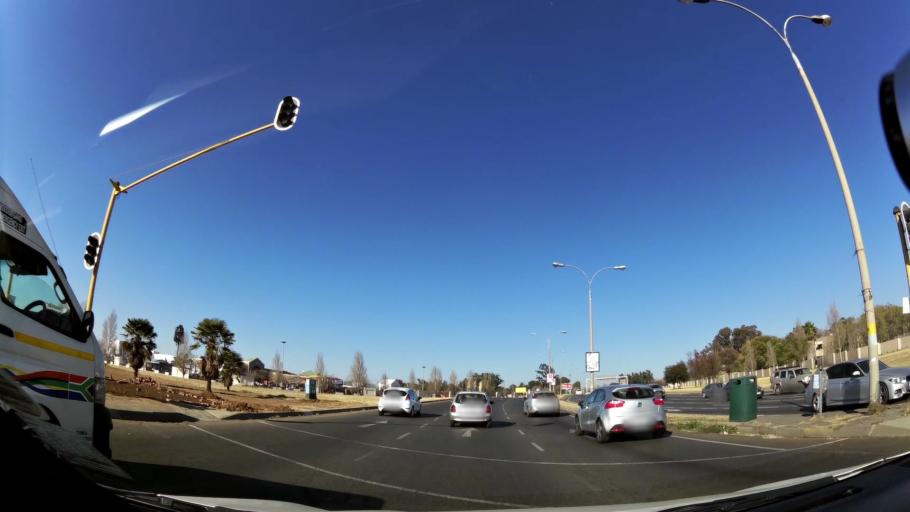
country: ZA
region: Gauteng
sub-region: Ekurhuleni Metropolitan Municipality
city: Germiston
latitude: -26.2783
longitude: 28.1237
